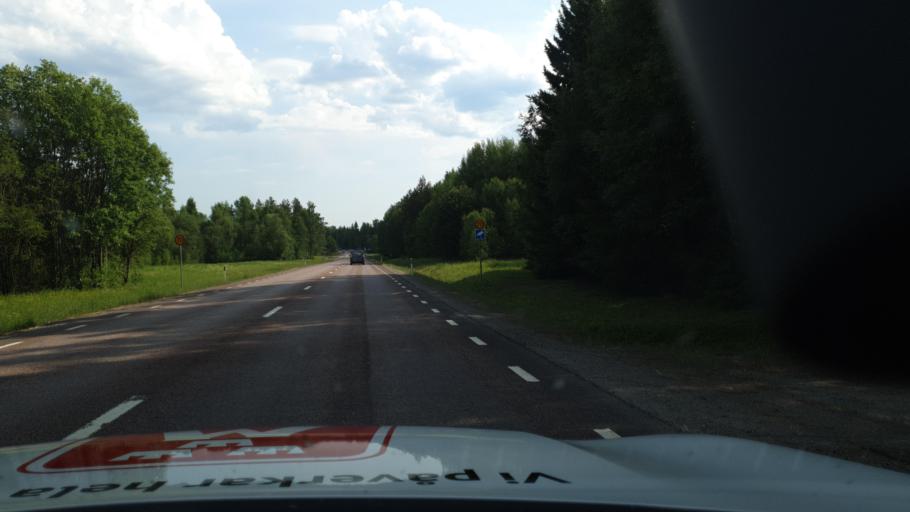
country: SE
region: Vaesterbotten
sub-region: Skelleftea Kommun
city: Burea
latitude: 64.6226
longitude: 21.1784
